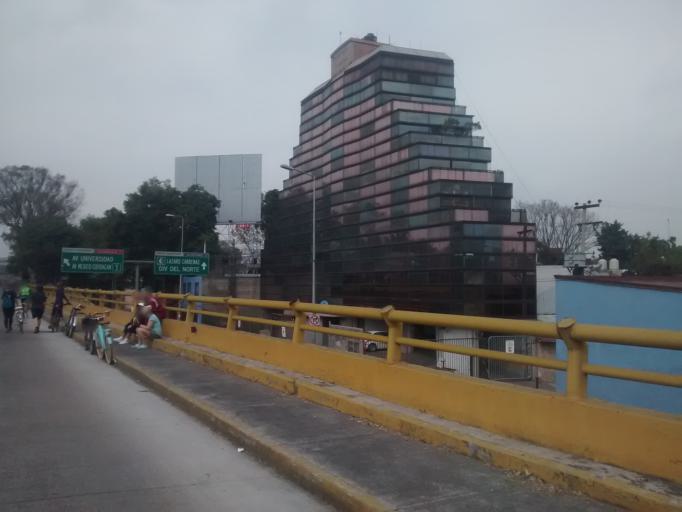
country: MX
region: Mexico City
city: Coyoacan
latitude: 19.3575
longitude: -99.1461
